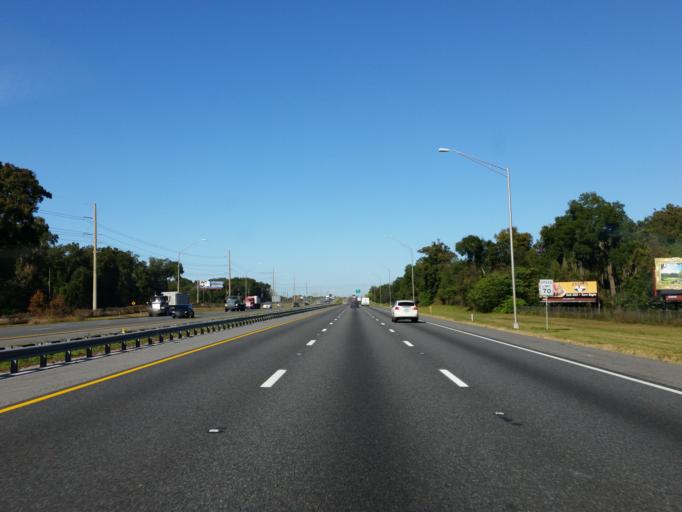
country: US
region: Florida
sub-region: Marion County
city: Ocala
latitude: 29.1601
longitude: -82.1848
